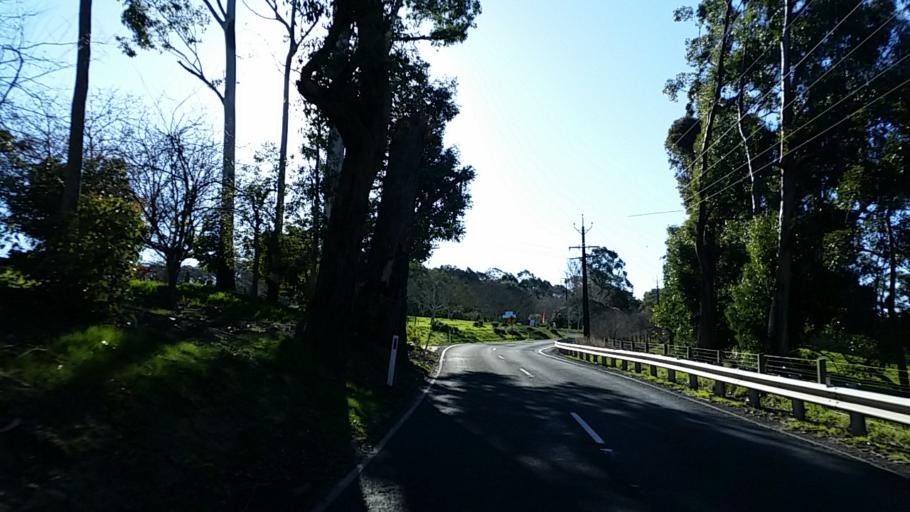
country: AU
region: South Australia
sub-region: Adelaide Hills
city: Crafers
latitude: -34.9578
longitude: 138.7200
